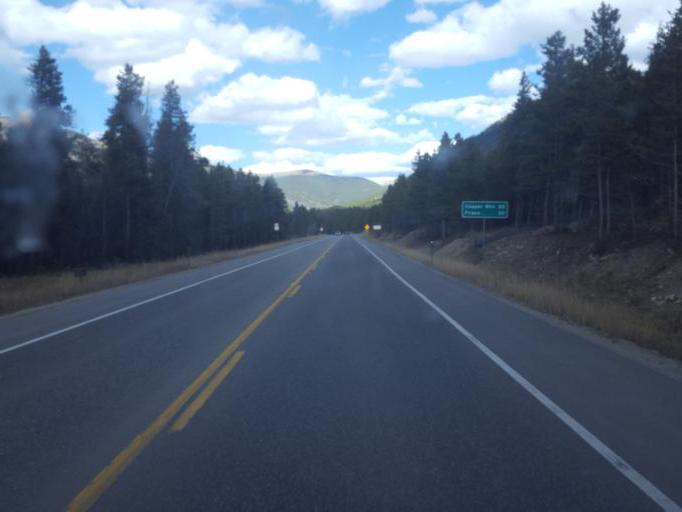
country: US
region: Colorado
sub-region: Lake County
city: Leadville North
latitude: 39.2700
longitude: -106.2894
